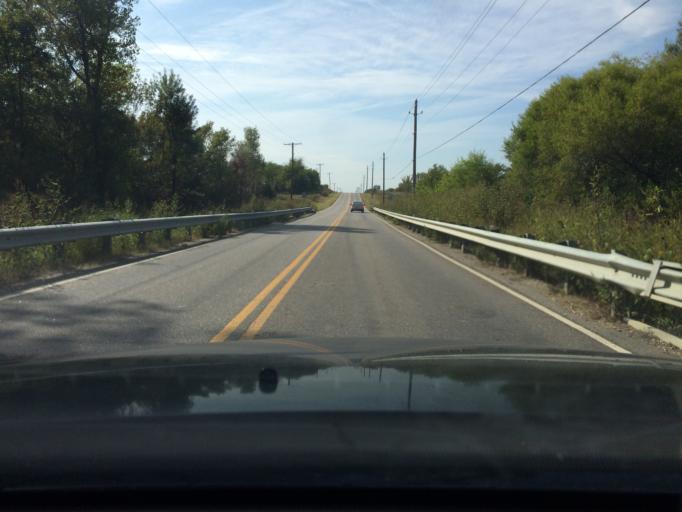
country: US
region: Oklahoma
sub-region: Tulsa County
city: Broken Arrow
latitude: 36.1045
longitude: -95.7974
